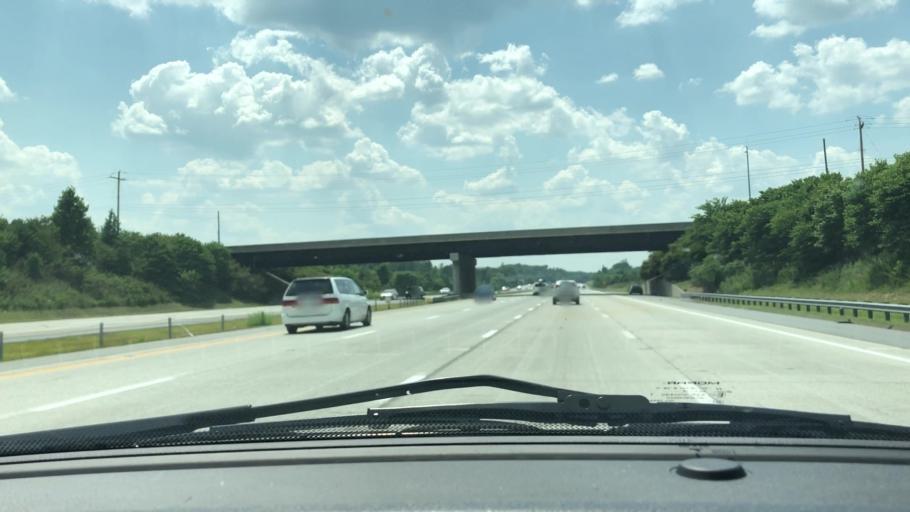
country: US
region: North Carolina
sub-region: Guilford County
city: Pleasant Garden
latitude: 36.0011
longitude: -79.7907
